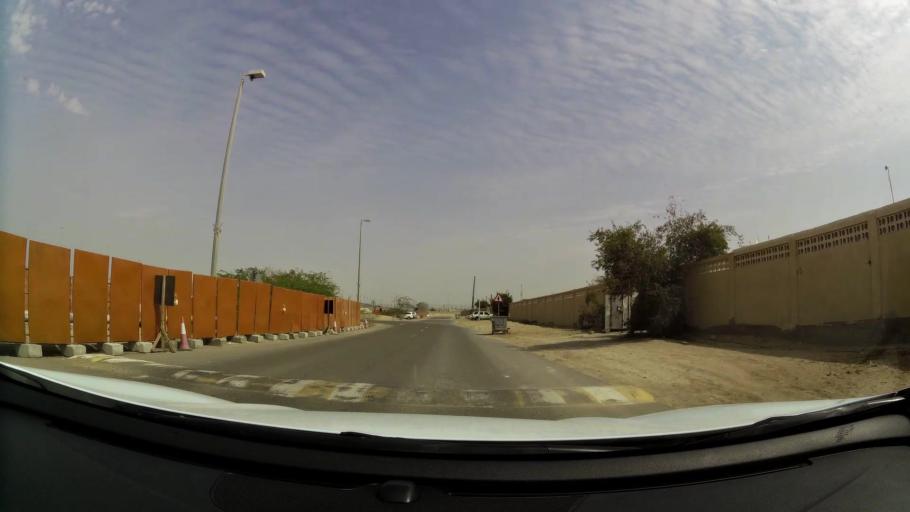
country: AE
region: Abu Dhabi
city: Abu Dhabi
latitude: 24.5640
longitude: 54.6828
